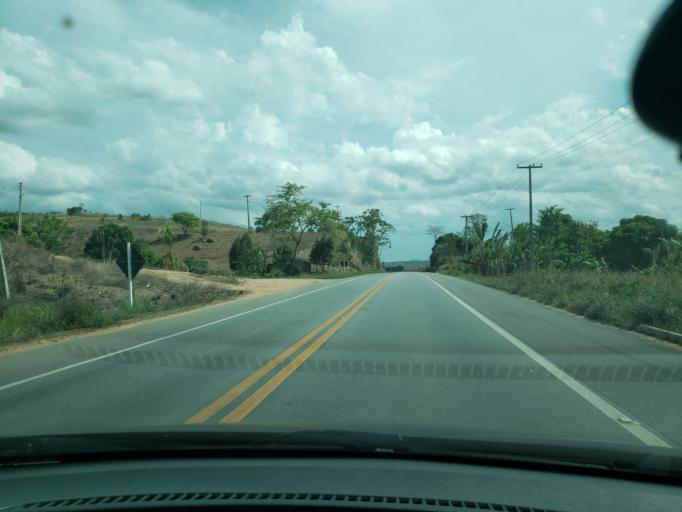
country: BR
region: Alagoas
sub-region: Murici
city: Murici
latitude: -9.2845
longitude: -35.9624
